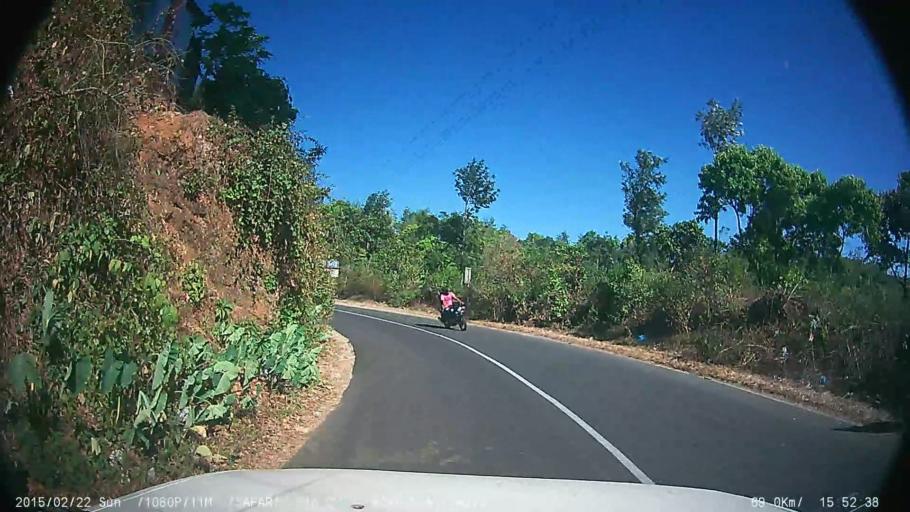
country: IN
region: Kerala
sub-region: Kottayam
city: Erattupetta
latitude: 9.5742
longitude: 77.0107
